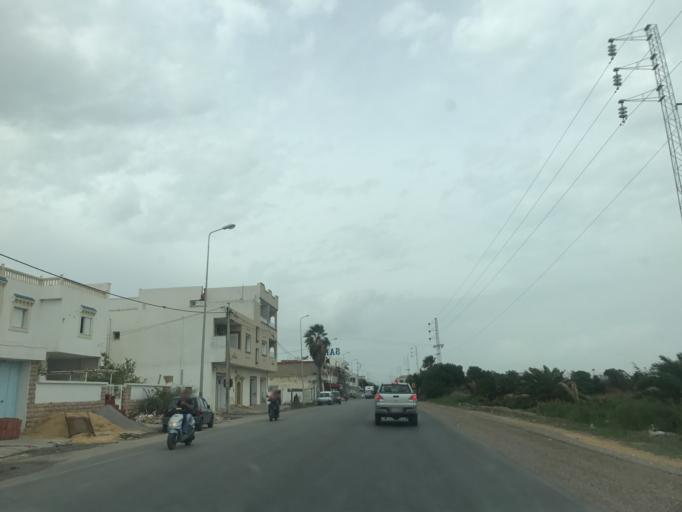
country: TN
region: Al Munastir
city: Banbalah
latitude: 35.7087
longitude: 10.8224
